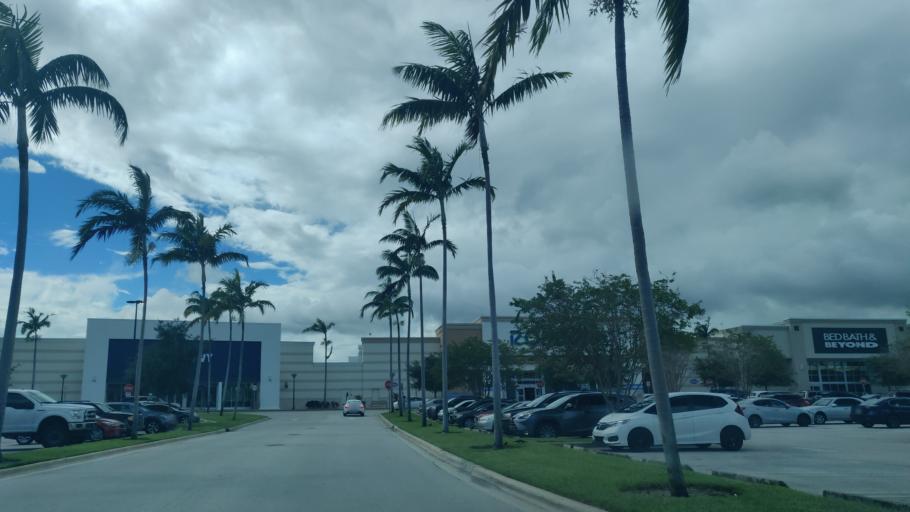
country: US
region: Florida
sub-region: Palm Beach County
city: Schall Circle
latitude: 26.7237
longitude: -80.0893
